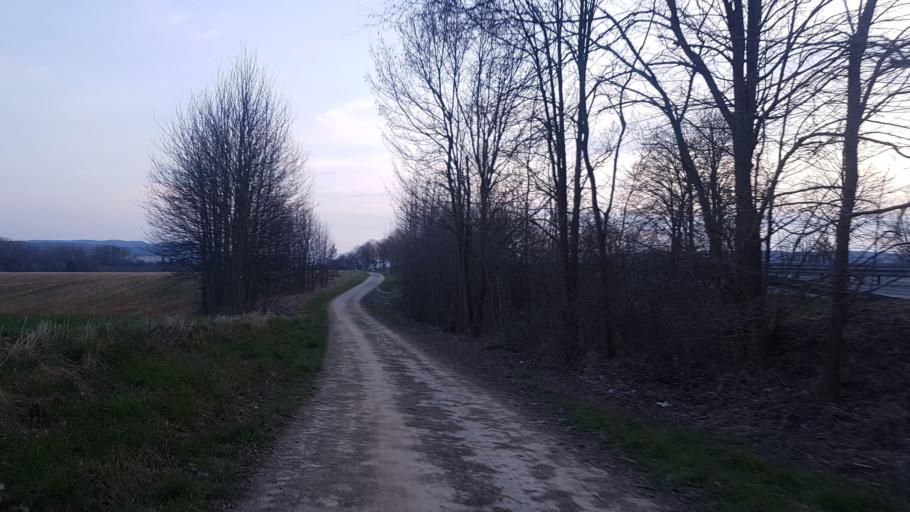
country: DE
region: Lower Saxony
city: Bad Munder am Deister
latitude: 52.1559
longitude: 9.4547
